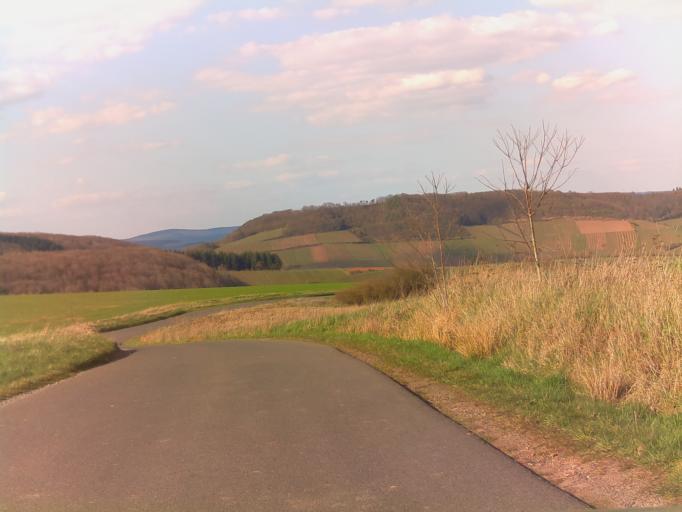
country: DE
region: Rheinland-Pfalz
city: Kirschroth
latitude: 49.7465
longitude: 7.5662
